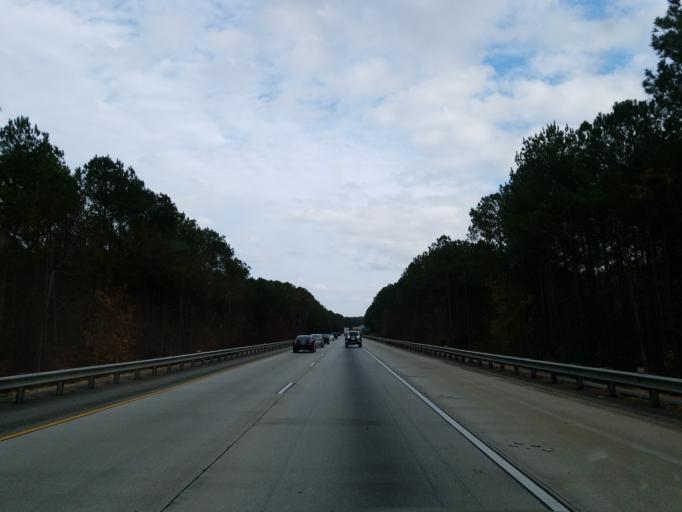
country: US
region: Georgia
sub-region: Carroll County
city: Mount Zion
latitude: 33.6887
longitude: -85.2128
